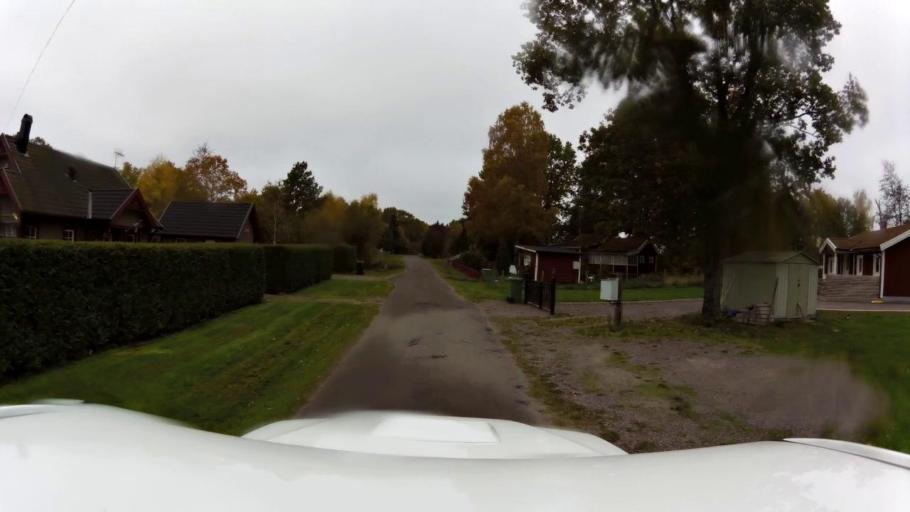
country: SE
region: OEstergoetland
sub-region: Linkopings Kommun
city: Linghem
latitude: 58.4973
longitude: 15.7408
